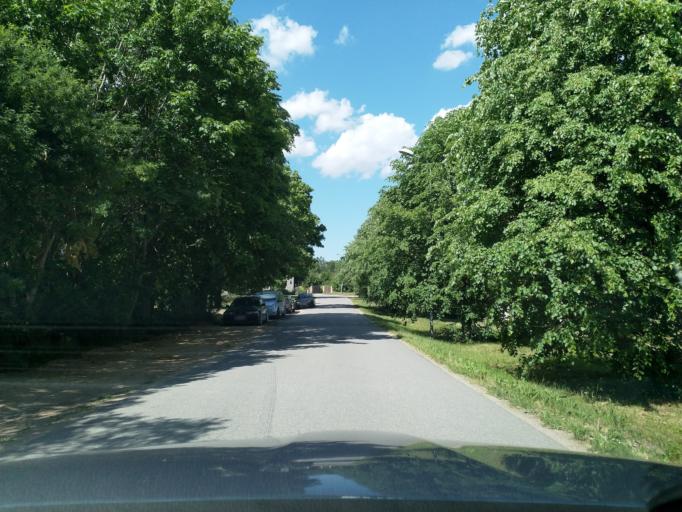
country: LV
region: Alsunga
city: Alsunga
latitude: 56.9777
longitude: 21.5654
